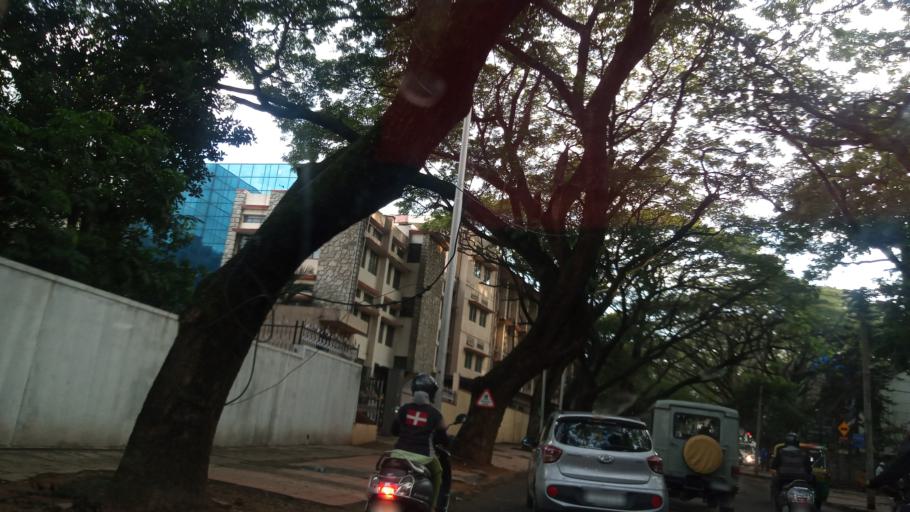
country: IN
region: Karnataka
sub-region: Bangalore Urban
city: Bangalore
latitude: 12.9257
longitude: 77.6287
